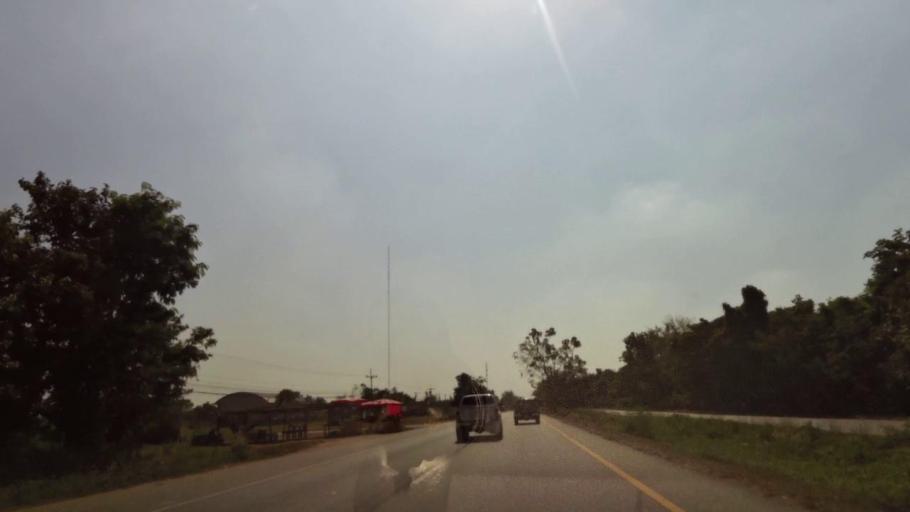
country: TH
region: Phichit
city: Wachira Barami
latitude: 16.4185
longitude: 100.1438
